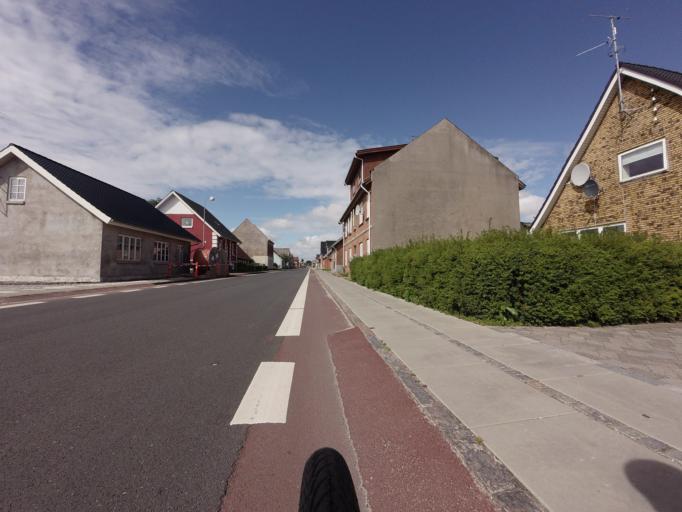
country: DK
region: Central Jutland
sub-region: Norddjurs Kommune
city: Allingabro
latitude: 56.4634
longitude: 10.3310
